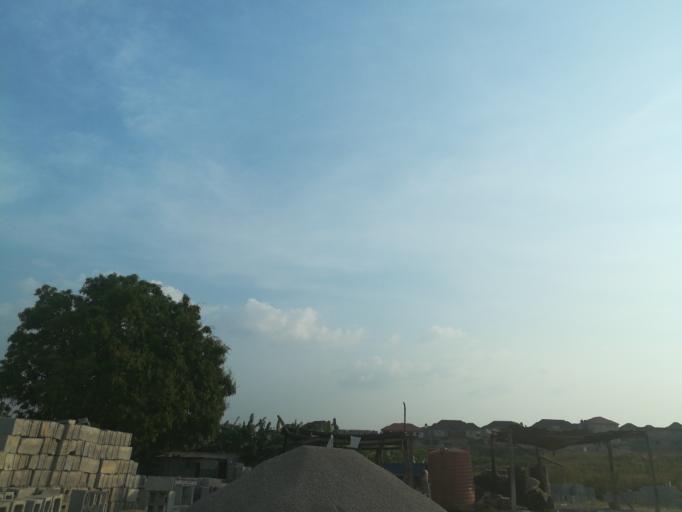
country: NG
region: Abuja Federal Capital Territory
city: Abuja
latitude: 9.1026
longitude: 7.3726
